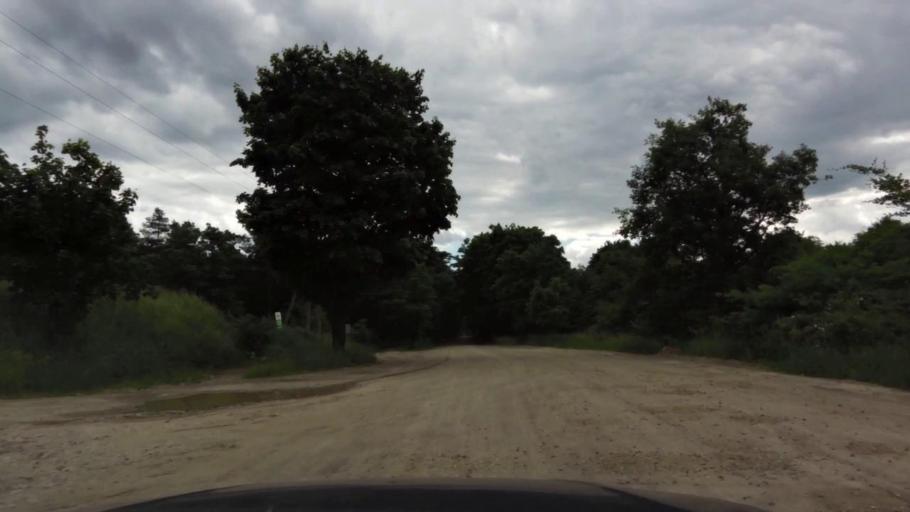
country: PL
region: West Pomeranian Voivodeship
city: Trzcinsko Zdroj
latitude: 52.8716
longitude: 14.5844
